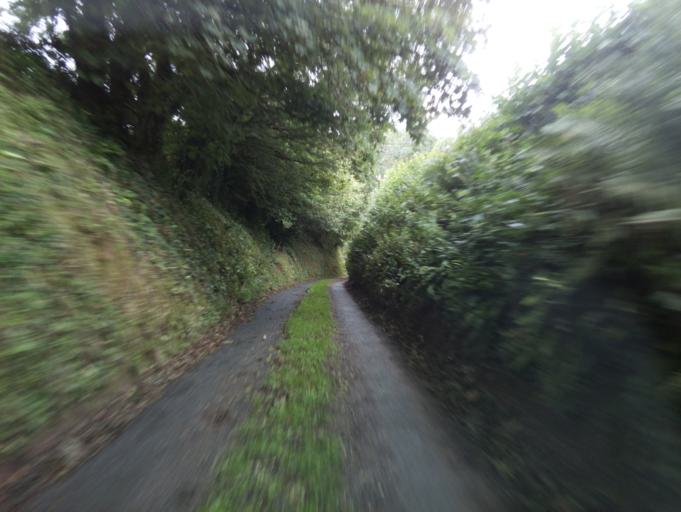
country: GB
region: England
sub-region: Devon
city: Dartmouth
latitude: 50.3466
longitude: -3.6193
